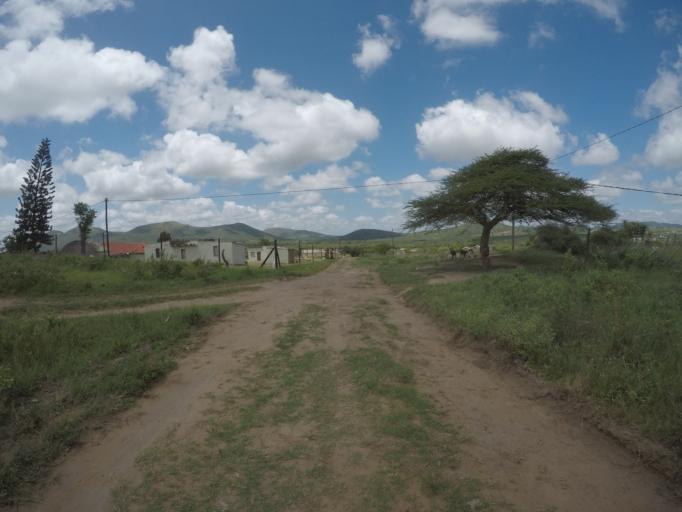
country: ZA
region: KwaZulu-Natal
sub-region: uThungulu District Municipality
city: Empangeni
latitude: -28.5822
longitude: 31.8441
